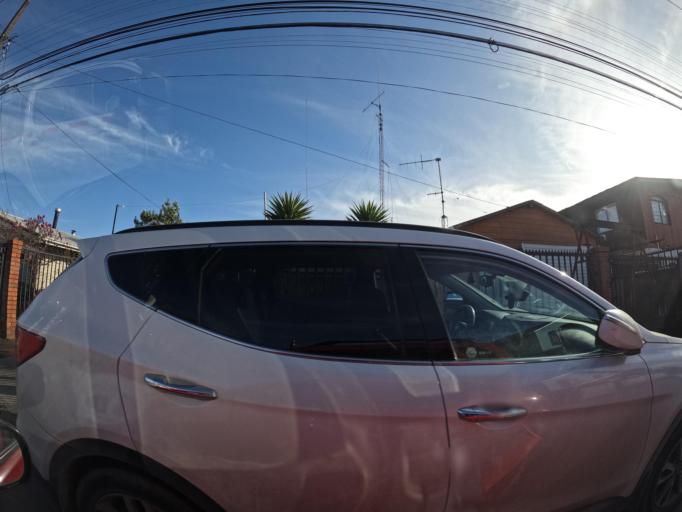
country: CL
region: Biobio
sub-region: Provincia de Concepcion
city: Talcahuano
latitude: -36.7474
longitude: -73.0920
